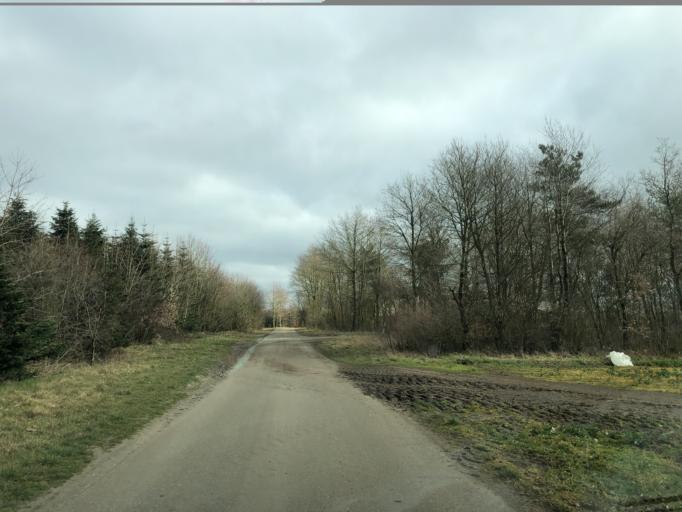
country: DK
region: South Denmark
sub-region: Billund Kommune
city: Billund
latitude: 55.7831
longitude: 9.1520
